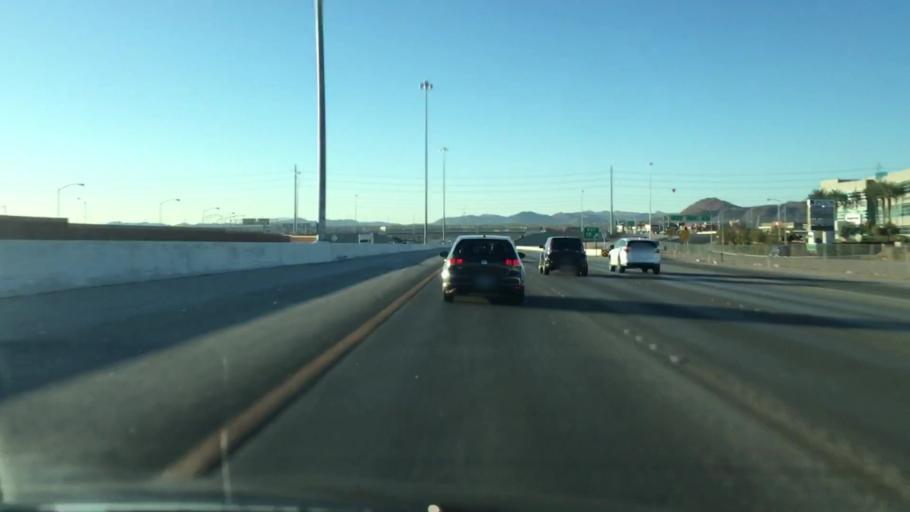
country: US
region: Nevada
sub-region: Clark County
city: Spring Valley
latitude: 36.0900
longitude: -115.2889
